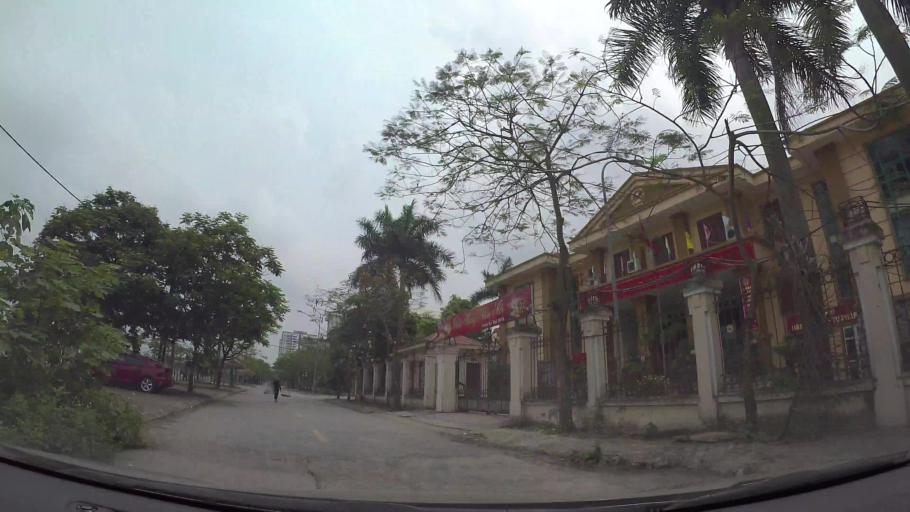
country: VN
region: Ha Noi
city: Trau Quy
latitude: 21.0697
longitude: 105.9104
